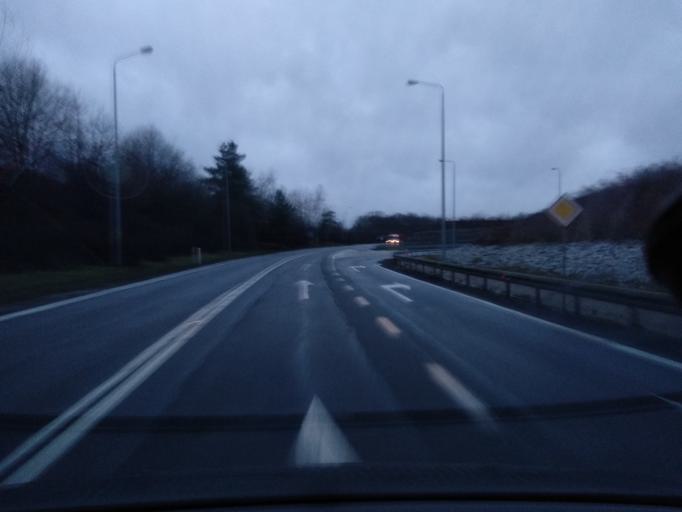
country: PL
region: Lower Silesian Voivodeship
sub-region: Powiat legnicki
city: Prochowice
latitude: 51.2722
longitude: 16.3534
